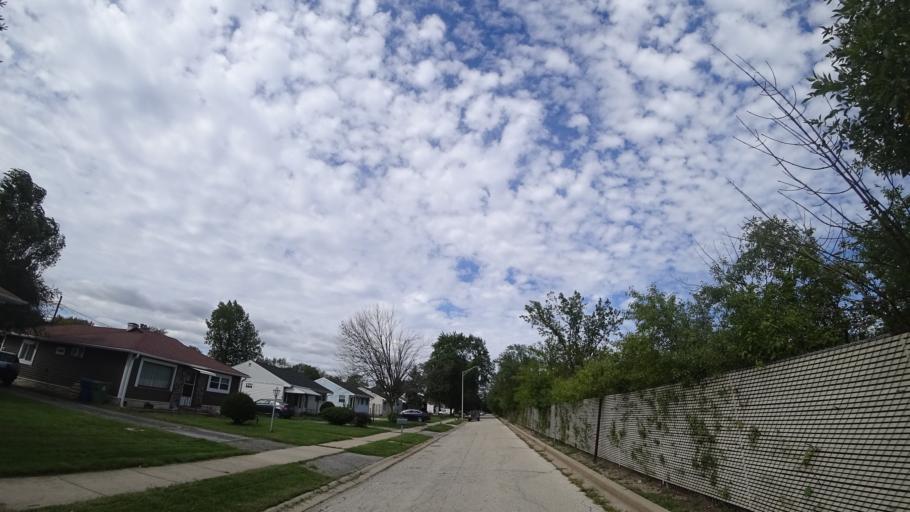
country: US
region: Illinois
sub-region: Cook County
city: Chicago Ridge
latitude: 41.7160
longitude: -87.7847
